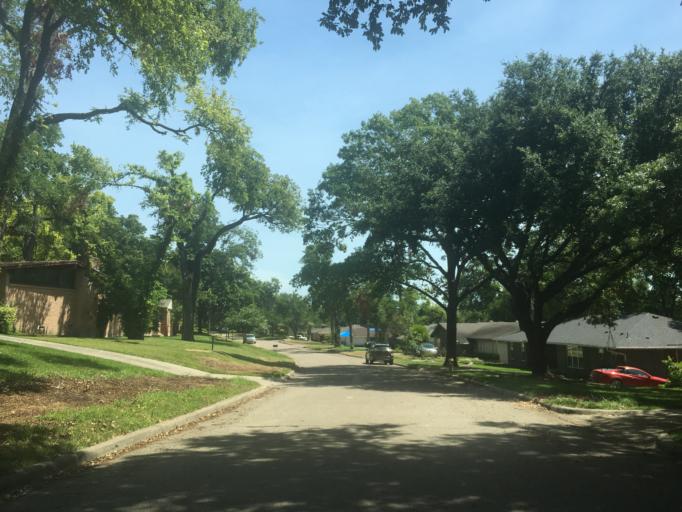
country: US
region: Texas
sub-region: Dallas County
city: Highland Park
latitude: 32.8699
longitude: -96.7372
